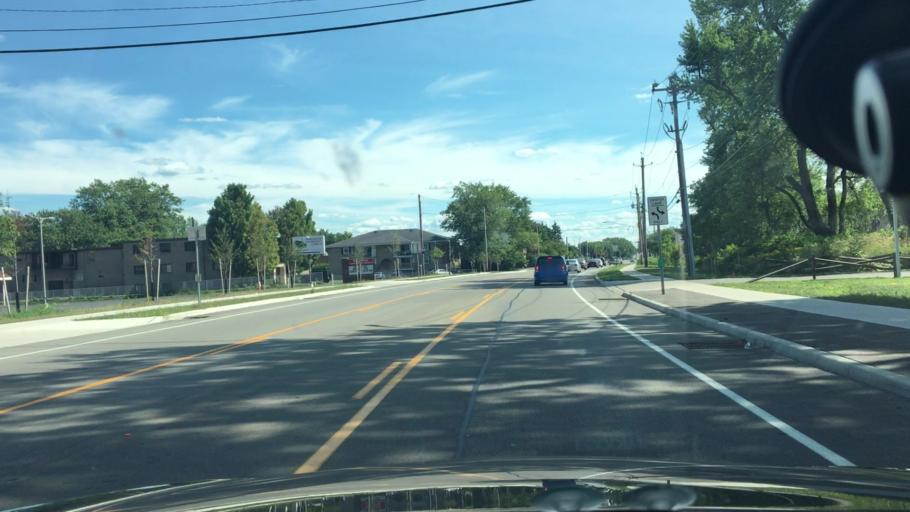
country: US
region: New York
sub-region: Erie County
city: West Seneca
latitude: 42.8685
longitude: -78.7872
